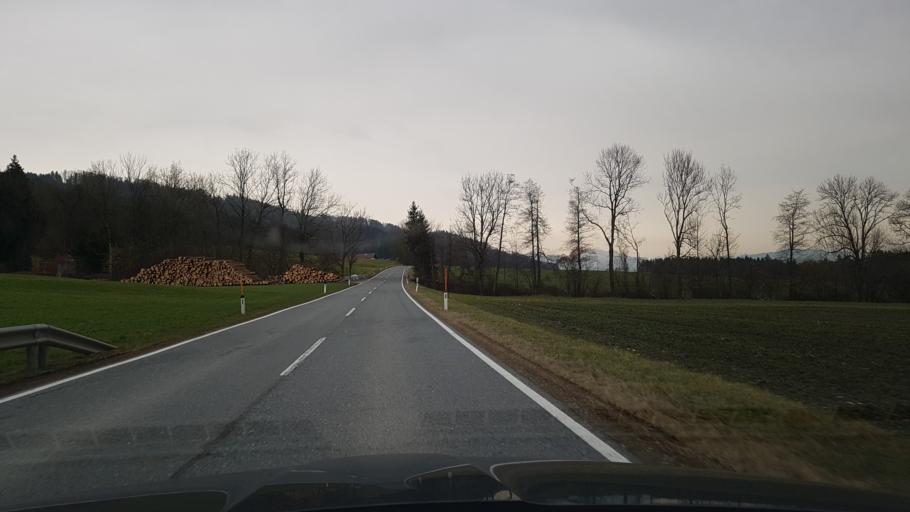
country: AT
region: Salzburg
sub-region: Politischer Bezirk Salzburg-Umgebung
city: Nussdorf am Haunsberg
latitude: 47.9466
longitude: 13.0013
